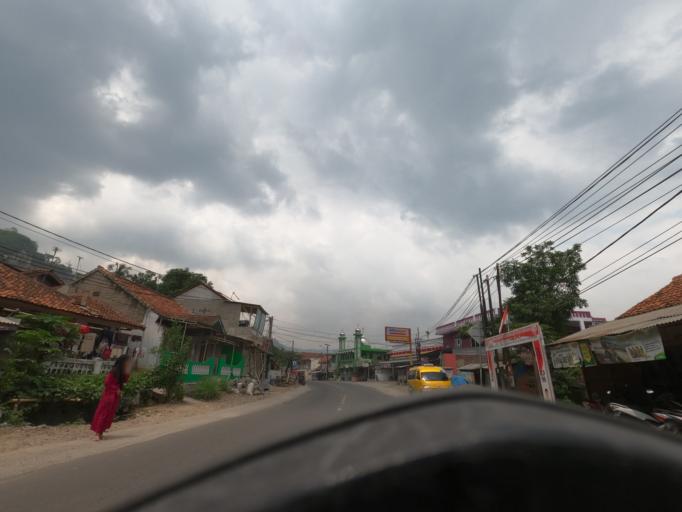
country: ID
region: West Java
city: Padalarang
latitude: -6.8320
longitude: 107.4287
